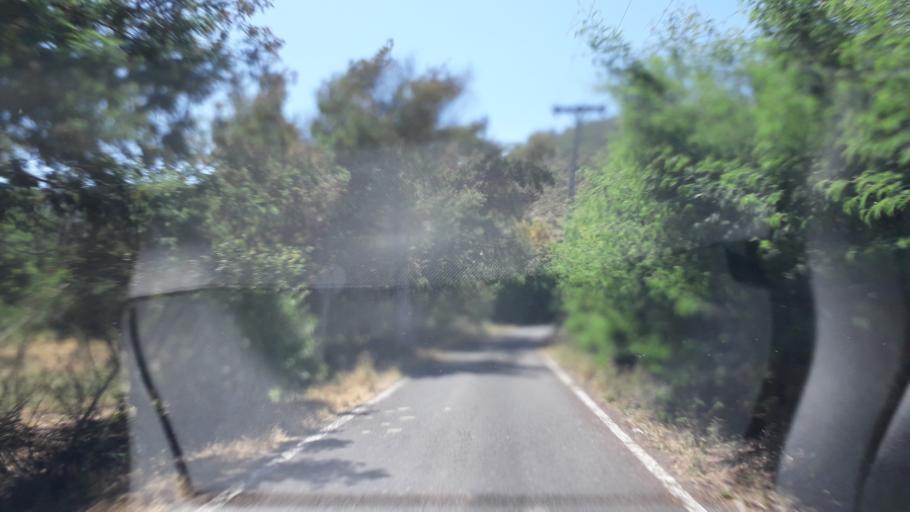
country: CL
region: Valparaiso
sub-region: Provincia de Marga Marga
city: Limache
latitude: -33.0744
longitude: -71.2125
